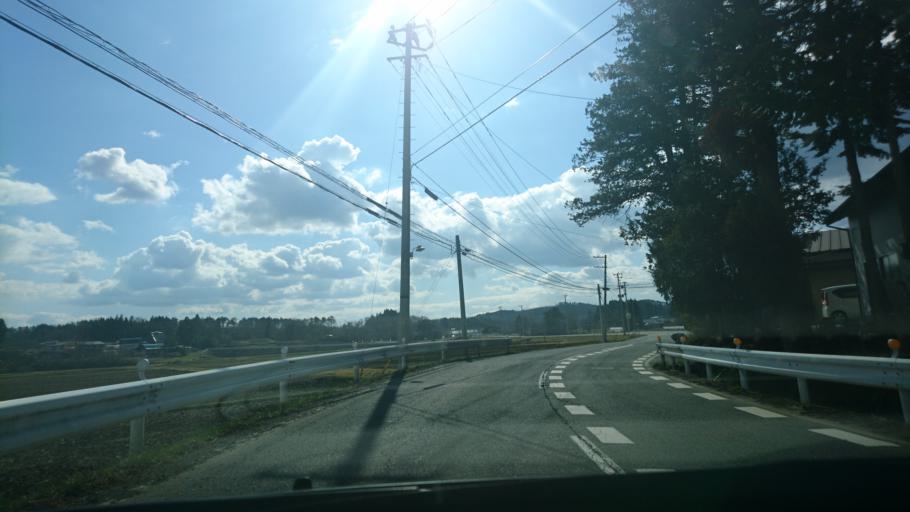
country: JP
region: Iwate
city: Kitakami
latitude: 39.2364
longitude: 141.1954
